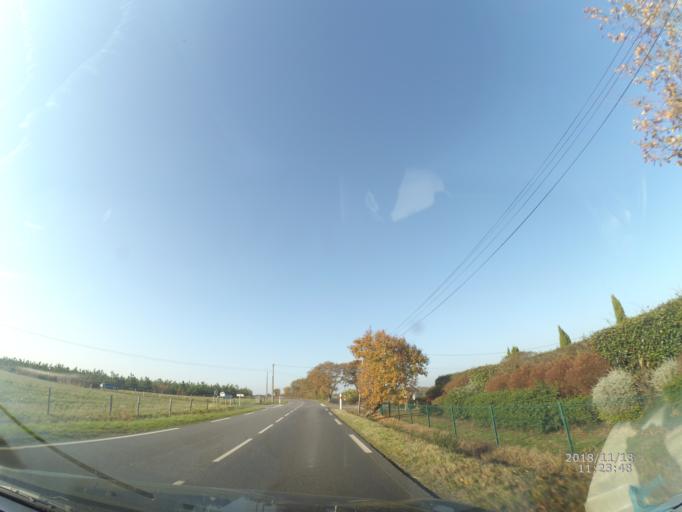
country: FR
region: Pays de la Loire
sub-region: Departement de la Loire-Atlantique
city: Saint-Pere-en-Retz
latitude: 47.2200
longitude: -2.0961
